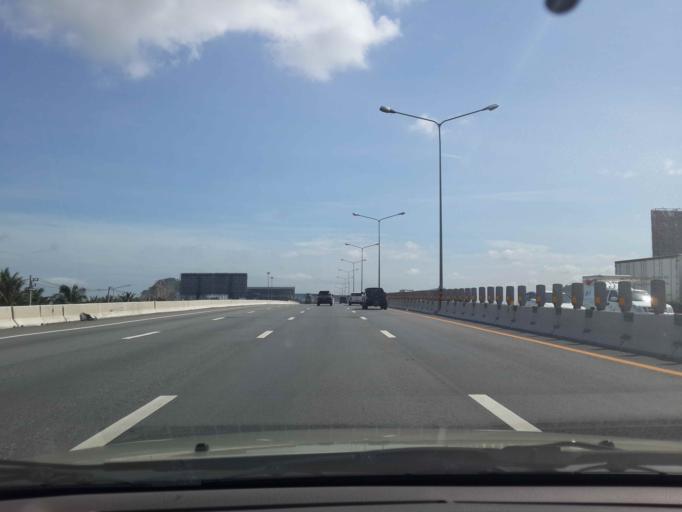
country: TH
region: Chon Buri
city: Chon Buri
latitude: 13.2807
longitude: 100.9908
